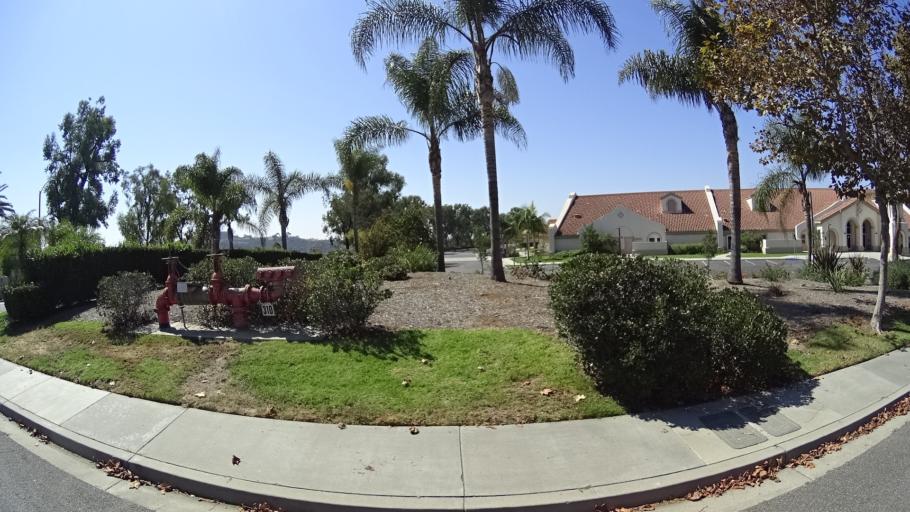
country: US
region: California
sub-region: Orange County
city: San Clemente
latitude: 33.4447
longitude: -117.5937
